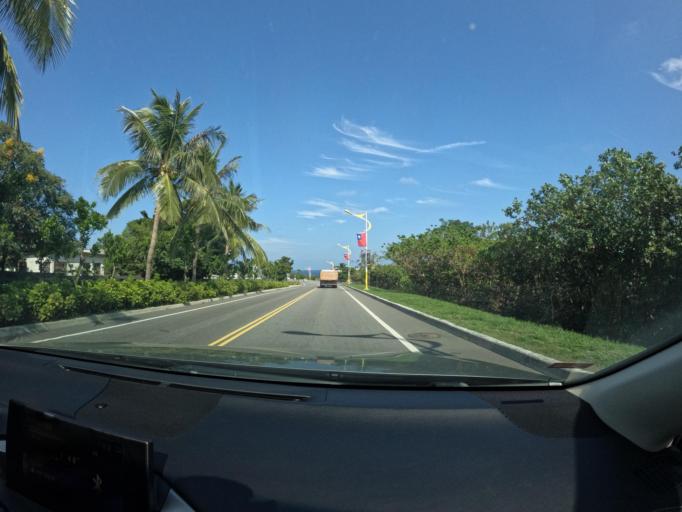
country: TW
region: Taiwan
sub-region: Hualien
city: Hualian
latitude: 23.9894
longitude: 121.6315
